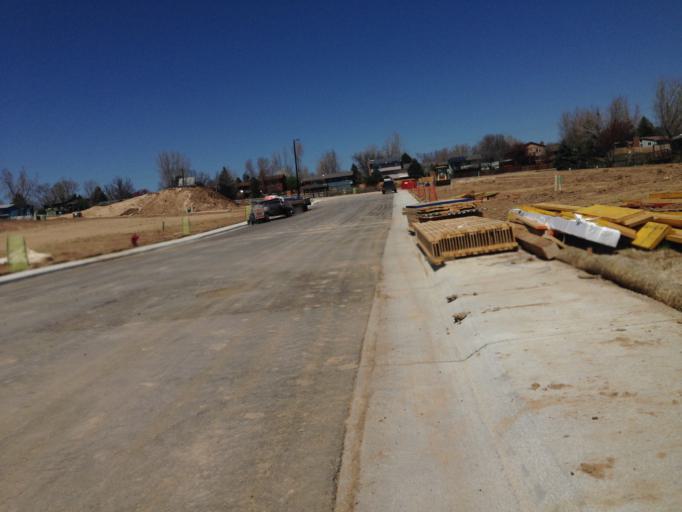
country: US
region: Colorado
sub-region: Boulder County
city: Louisville
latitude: 39.9890
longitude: -105.1165
